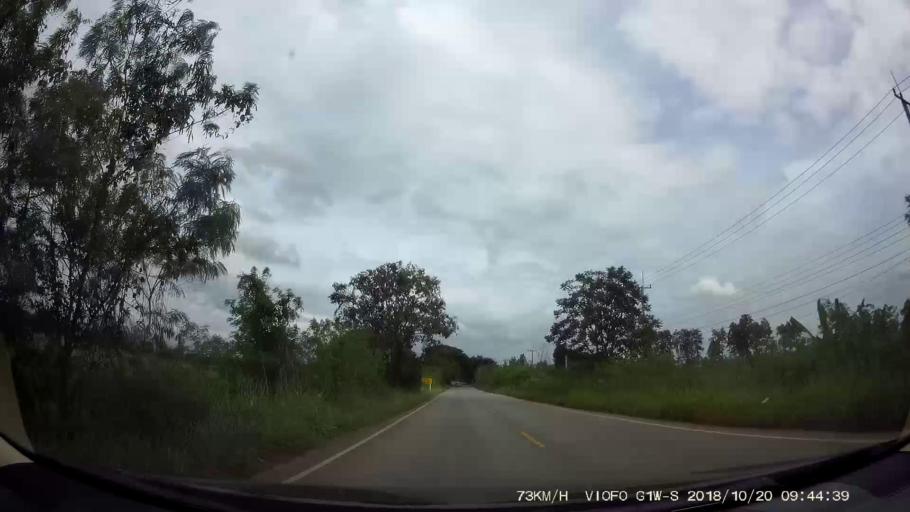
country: TH
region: Chaiyaphum
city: Khon San
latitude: 16.4854
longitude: 101.9429
